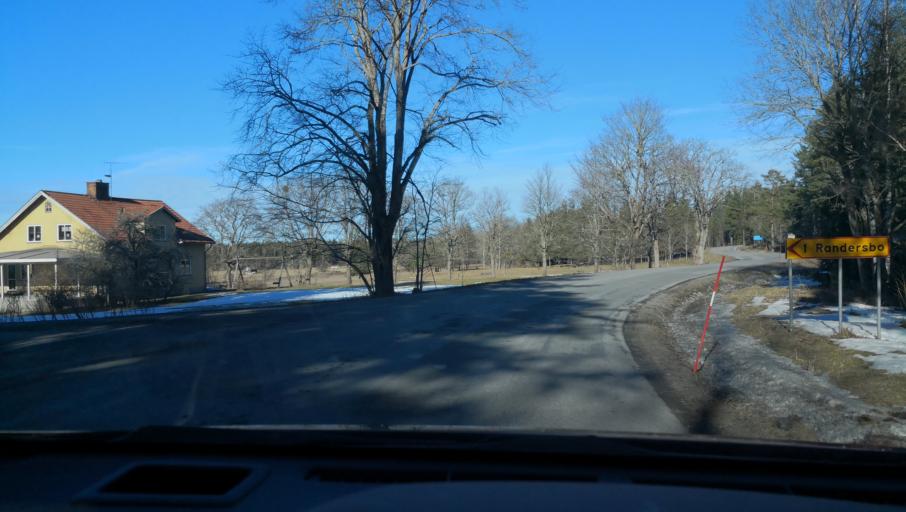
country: SE
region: Uppsala
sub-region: Osthammars Kommun
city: Osterbybruk
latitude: 60.2540
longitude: 17.9455
